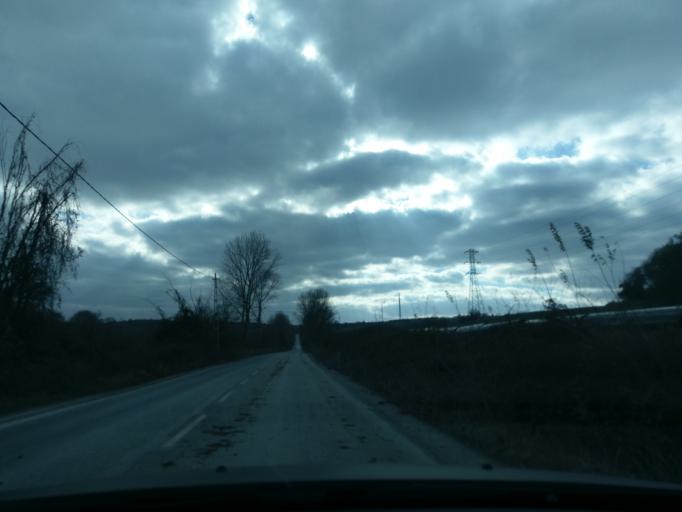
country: TR
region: Istanbul
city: Durusu
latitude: 41.2888
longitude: 28.6643
